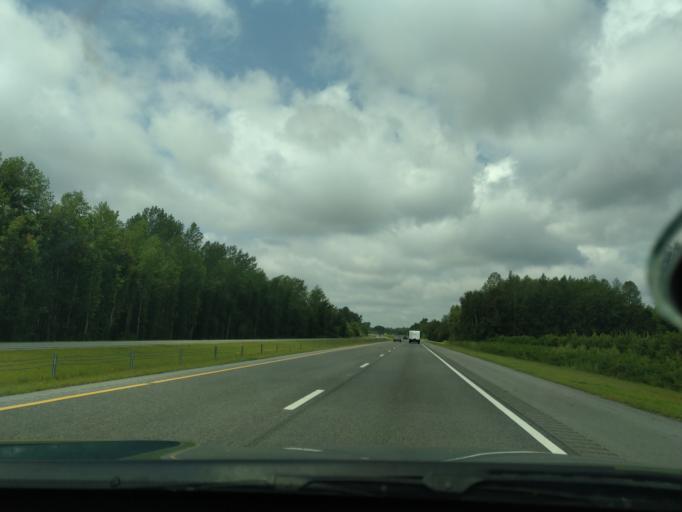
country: US
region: North Carolina
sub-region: Martin County
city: Robersonville
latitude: 35.8332
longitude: -77.3053
